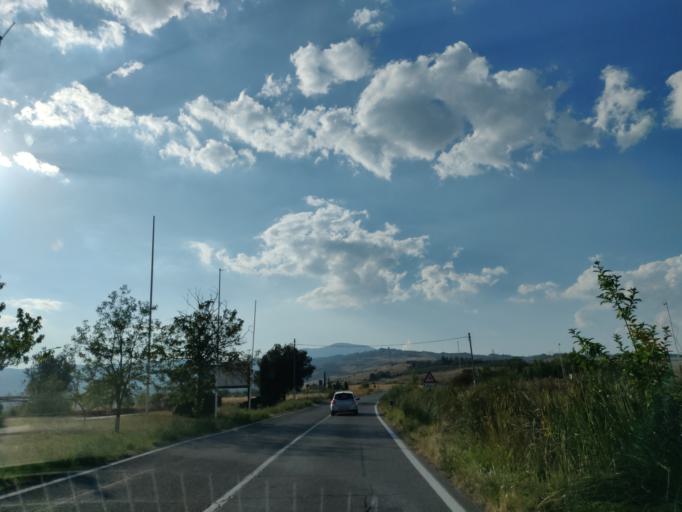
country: IT
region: Tuscany
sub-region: Provincia di Siena
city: Piancastagnaio
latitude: 42.8251
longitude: 11.7250
